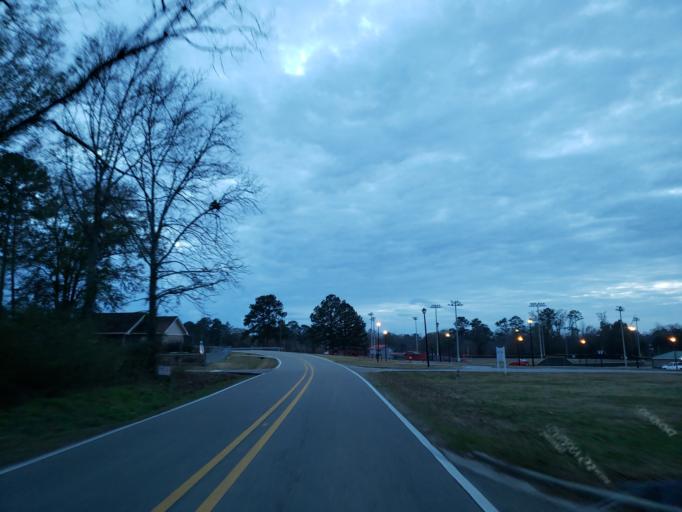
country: US
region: Mississippi
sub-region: Forrest County
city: Petal
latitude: 31.3424
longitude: -89.2493
